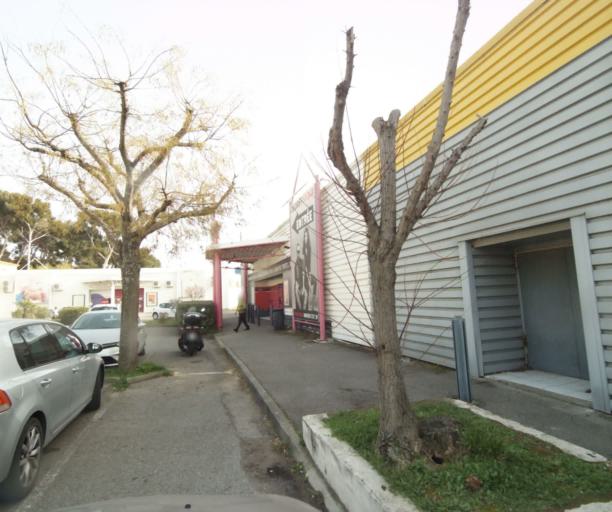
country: FR
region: Provence-Alpes-Cote d'Azur
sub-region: Departement des Bouches-du-Rhone
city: Vitrolles
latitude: 43.4341
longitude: 5.2624
